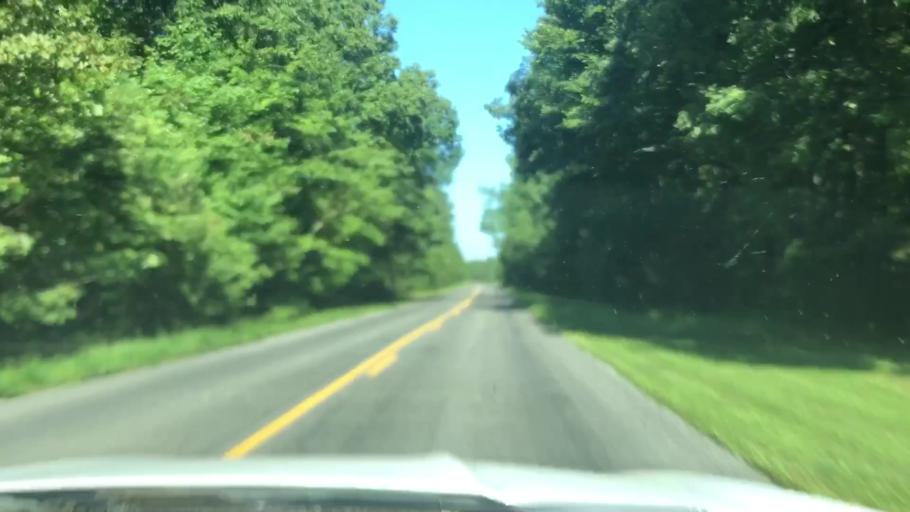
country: US
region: Virginia
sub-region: New Kent County
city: New Kent
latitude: 37.4842
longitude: -76.9284
